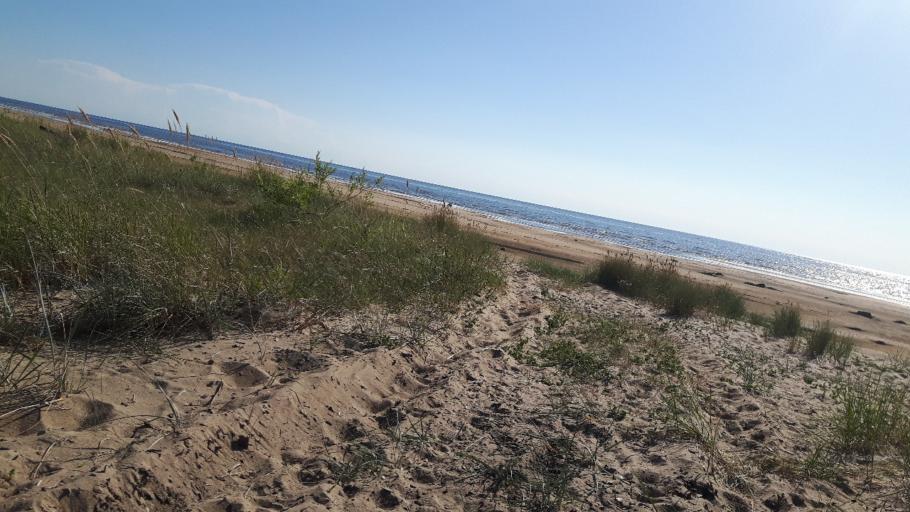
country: LV
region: Salacgrivas
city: Salacgriva
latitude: 57.7091
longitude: 24.3441
